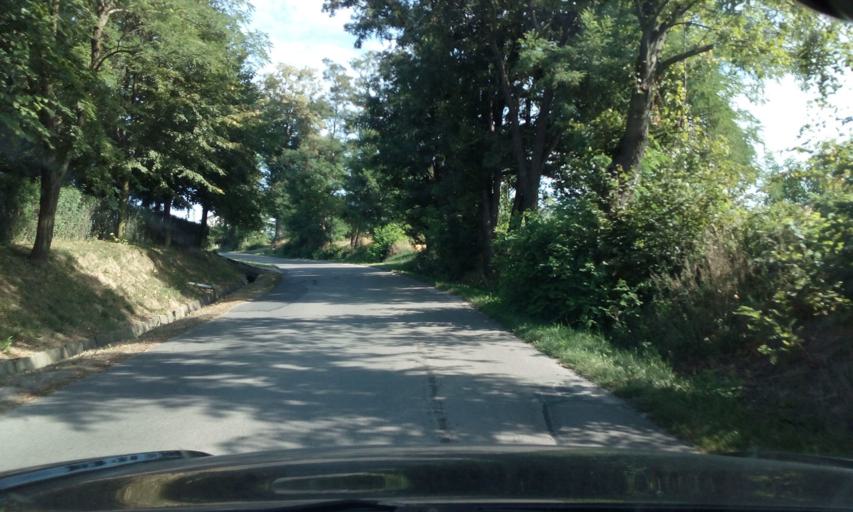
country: PL
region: Subcarpathian Voivodeship
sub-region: Powiat lancucki
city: Lancut
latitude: 50.0510
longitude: 22.2398
